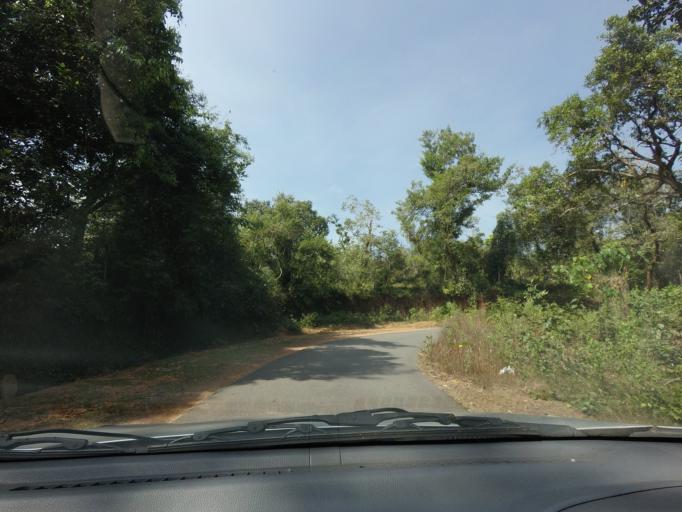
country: IN
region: Karnataka
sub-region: Kodagu
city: Somvarpet
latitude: 12.6872
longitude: 75.6154
